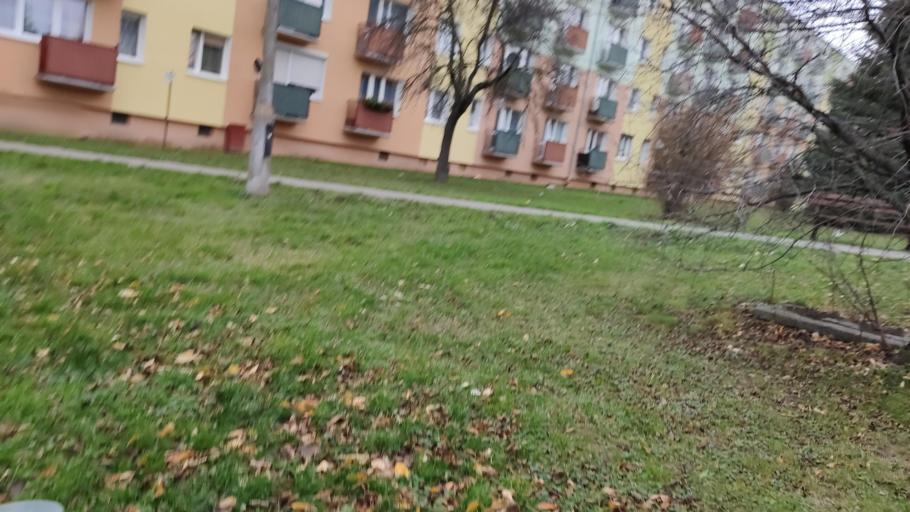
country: PL
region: Kujawsko-Pomorskie
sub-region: Powiat zninski
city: Barcin
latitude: 52.8527
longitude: 17.9444
